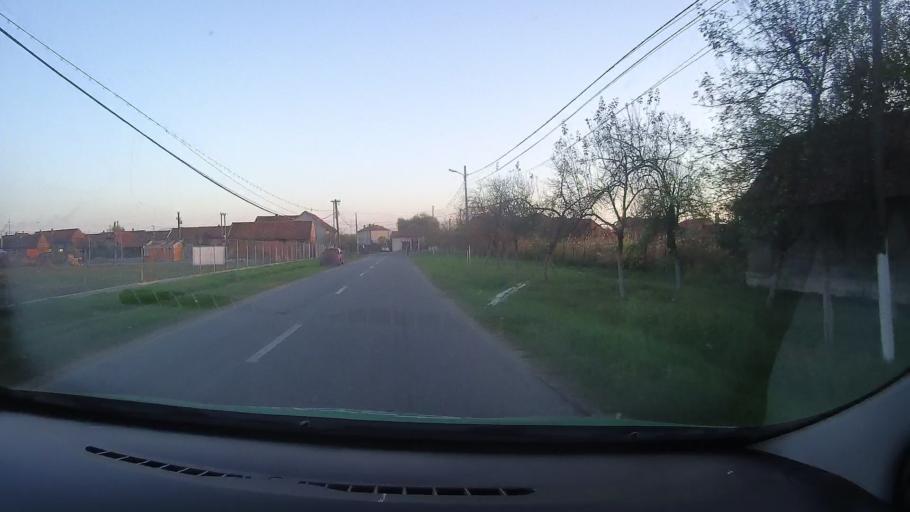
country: RO
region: Timis
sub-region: Comuna Manastiur
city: Manastiur
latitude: 45.8317
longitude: 22.0659
